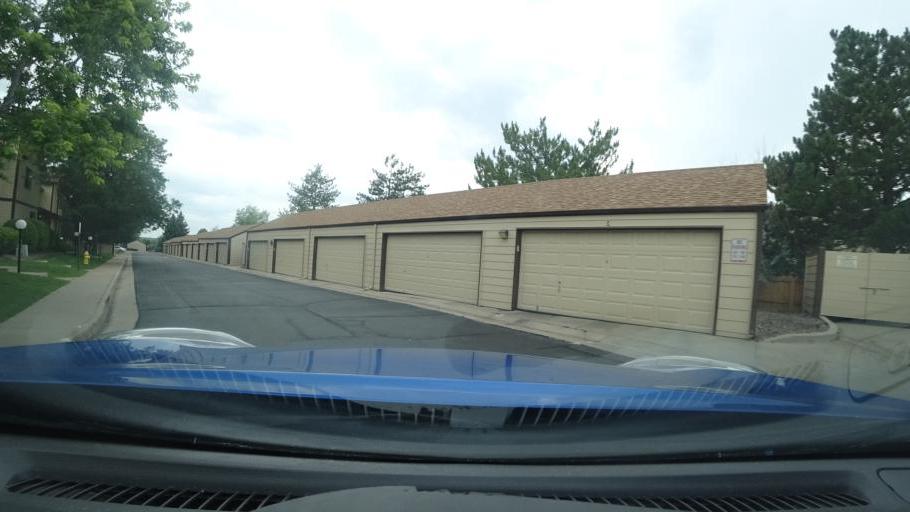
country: US
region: Colorado
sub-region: Adams County
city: Aurora
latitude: 39.6849
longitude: -104.7886
